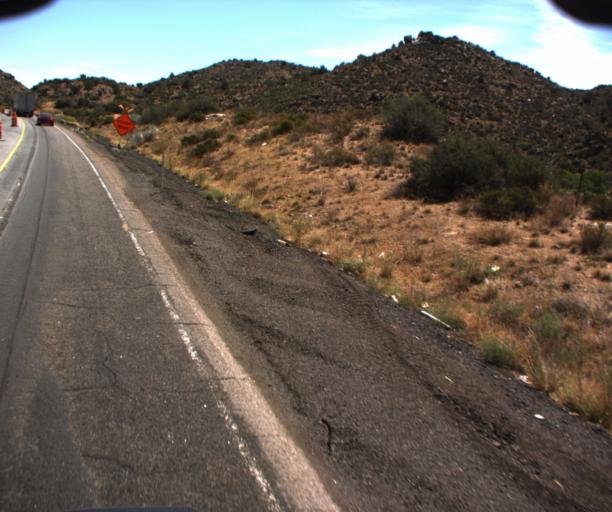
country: US
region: Arizona
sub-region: Mohave County
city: Peach Springs
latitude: 35.1728
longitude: -113.5034
